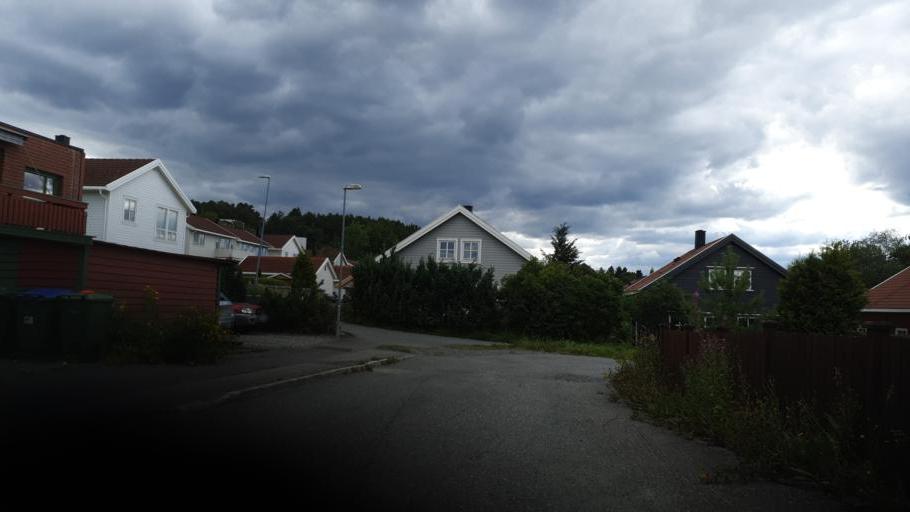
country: NO
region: Sor-Trondelag
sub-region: Malvik
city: Malvik
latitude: 63.4382
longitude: 10.5928
